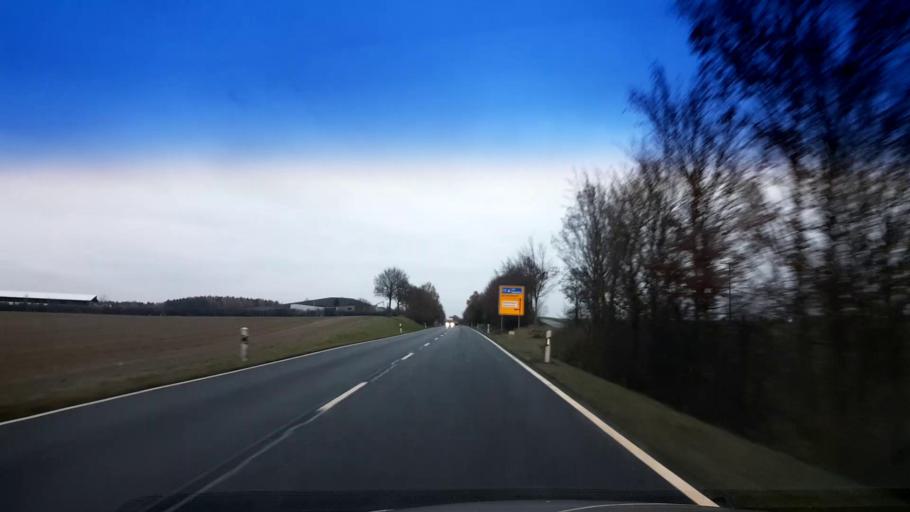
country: DE
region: Bavaria
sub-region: Upper Palatinate
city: Waldsassen
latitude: 49.9860
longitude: 12.2799
